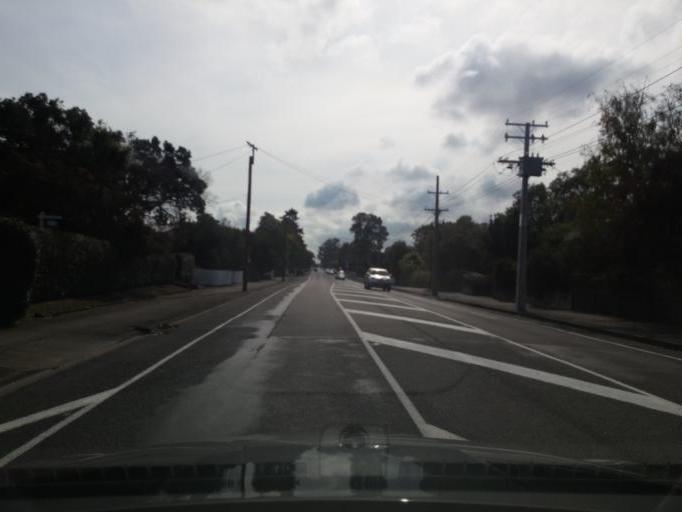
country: NZ
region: Wellington
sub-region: Masterton District
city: Masterton
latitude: -41.0867
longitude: 175.4533
